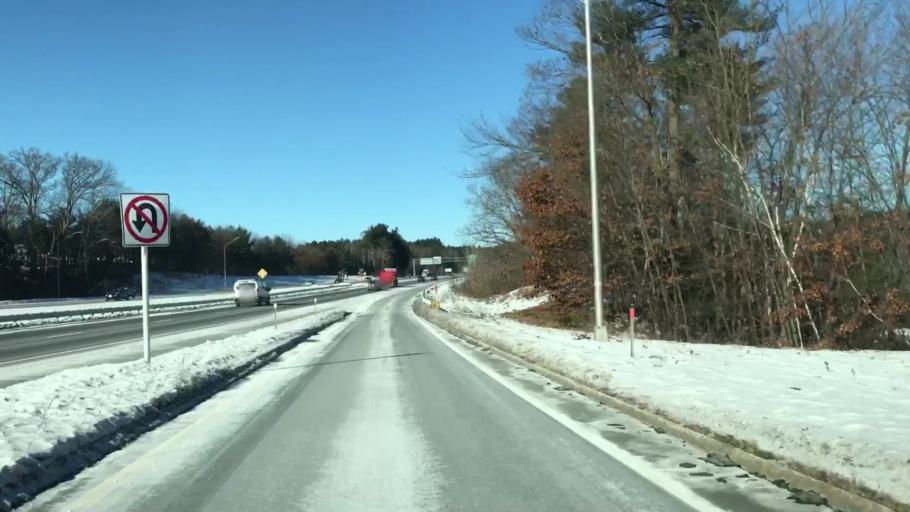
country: US
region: New Hampshire
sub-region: Hillsborough County
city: Bedford
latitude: 42.9524
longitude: -71.4799
